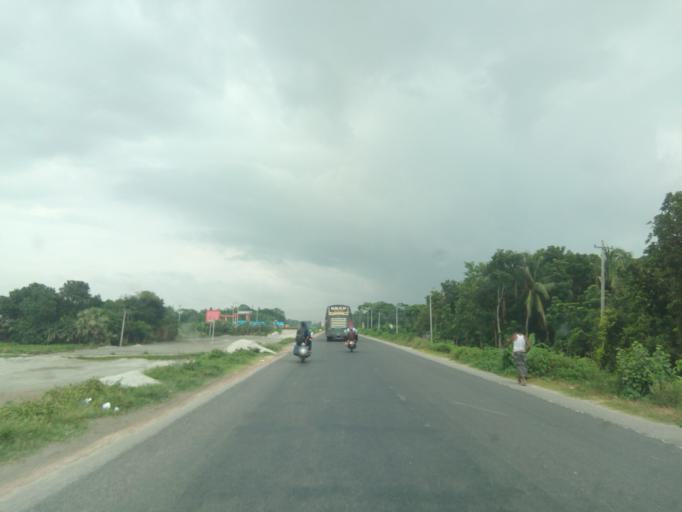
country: BD
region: Dhaka
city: Char Bhadrasan
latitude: 23.3697
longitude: 90.0590
